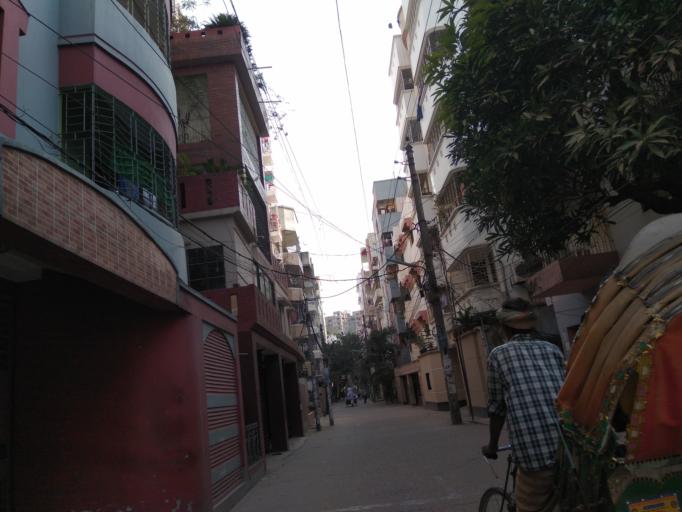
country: BD
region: Dhaka
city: Azimpur
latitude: 23.7725
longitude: 90.3572
